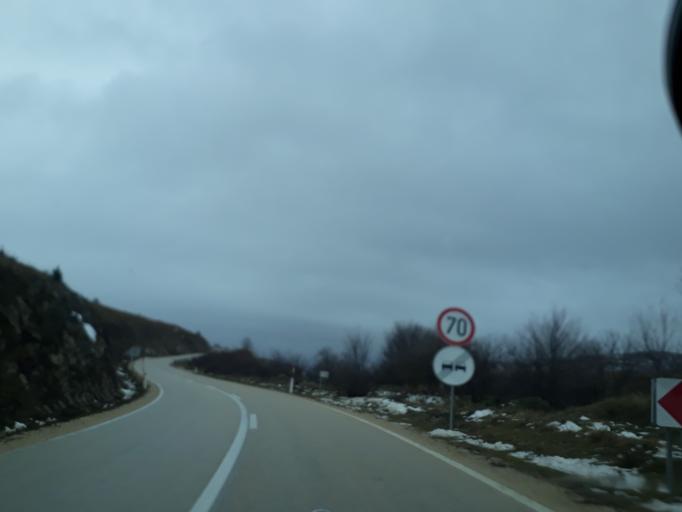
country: BA
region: Federation of Bosnia and Herzegovina
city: Tomislavgrad
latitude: 43.8211
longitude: 17.1933
